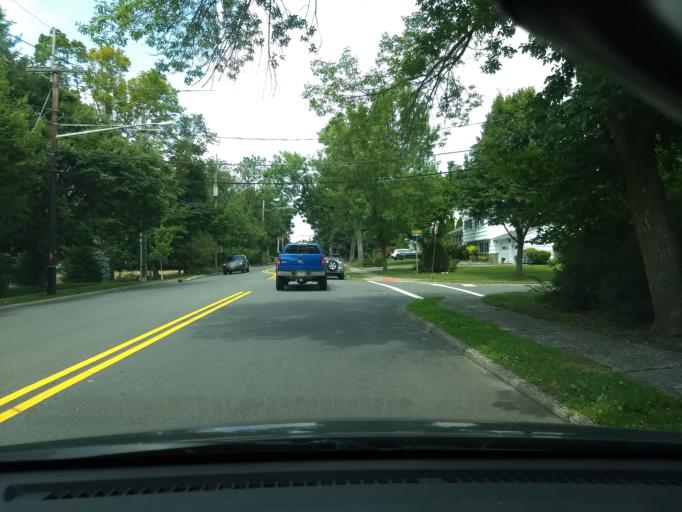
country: US
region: New Jersey
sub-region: Bergen County
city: Ho-Ho-Kus
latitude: 40.9794
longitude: -74.0888
